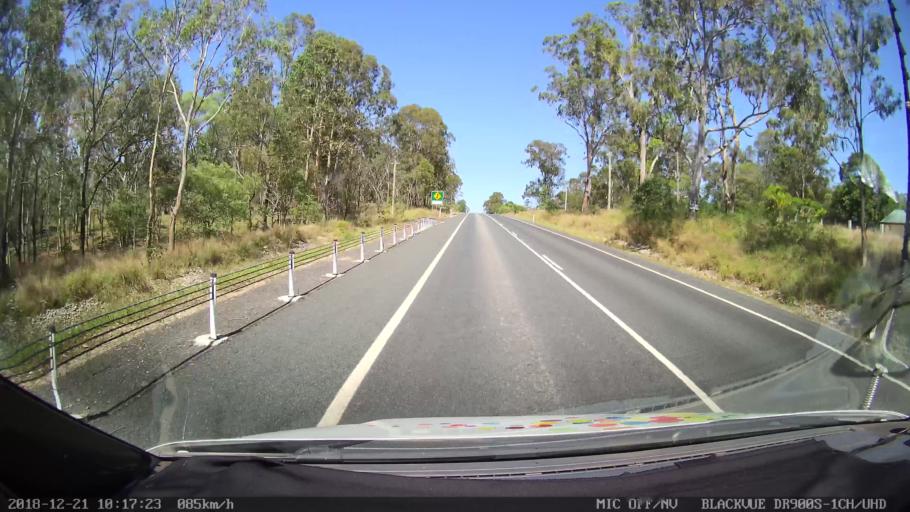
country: AU
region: New South Wales
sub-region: Clarence Valley
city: South Grafton
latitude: -29.6839
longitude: 152.8713
